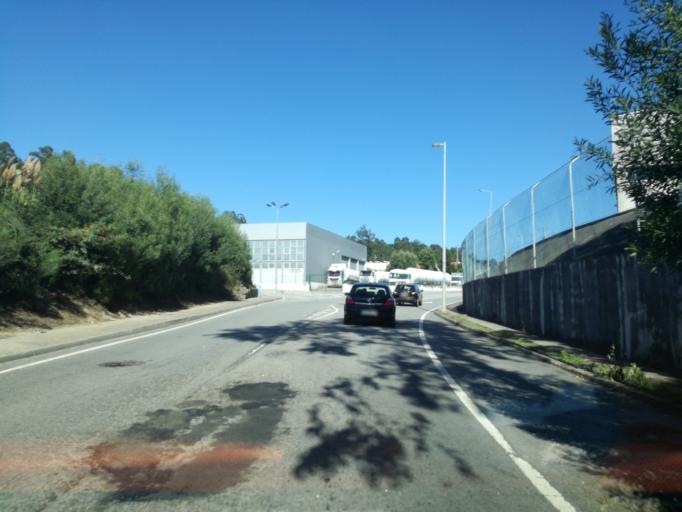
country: PT
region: Porto
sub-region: Trofa
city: Sao Romao do Coronado
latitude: 41.2856
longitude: -8.5967
